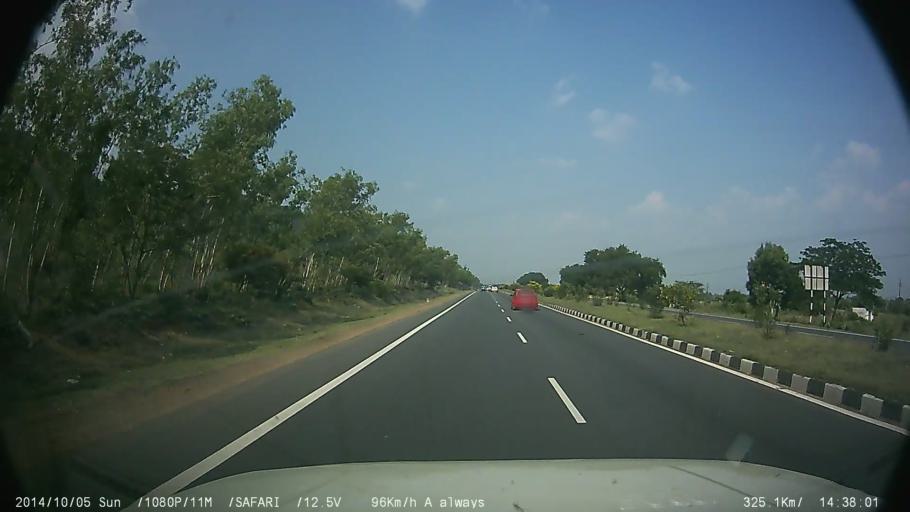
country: IN
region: Tamil Nadu
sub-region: Kancheepuram
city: Madurantakam
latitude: 12.3836
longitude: 79.7932
